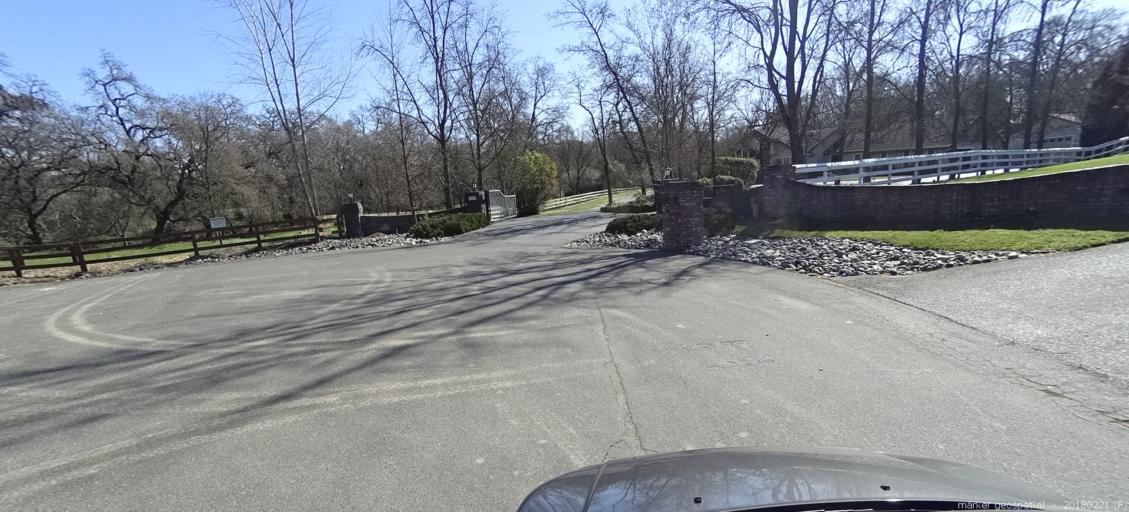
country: US
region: California
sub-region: Sacramento County
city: Orangevale
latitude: 38.7161
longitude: -121.2413
